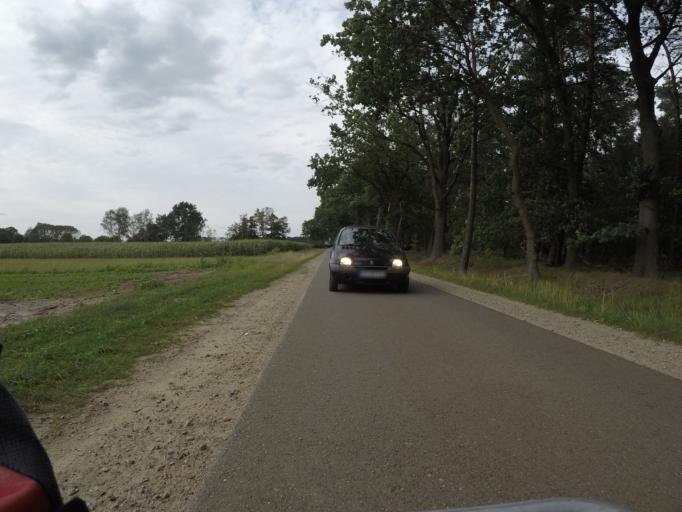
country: DE
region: Lower Saxony
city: Bardowick
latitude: 53.3088
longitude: 10.4026
